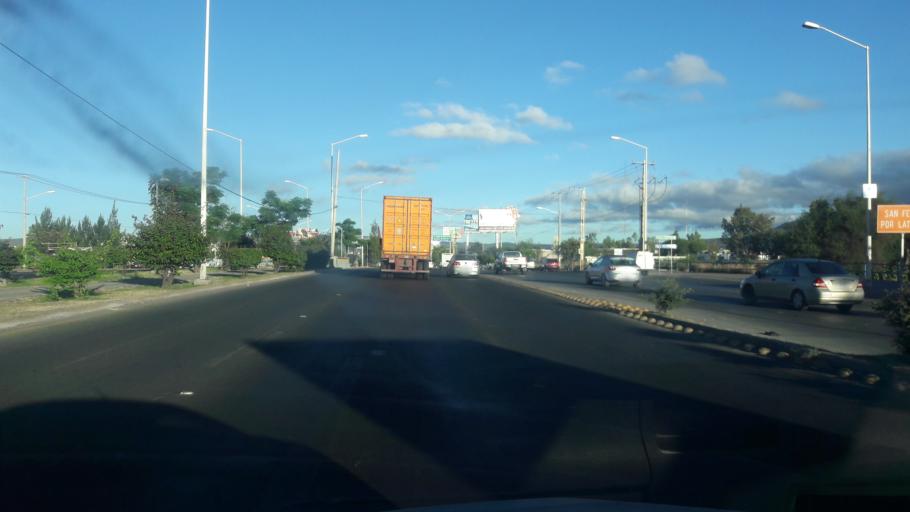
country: MX
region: Guanajuato
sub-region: Leon
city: Medina
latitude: 21.1679
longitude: -101.6537
